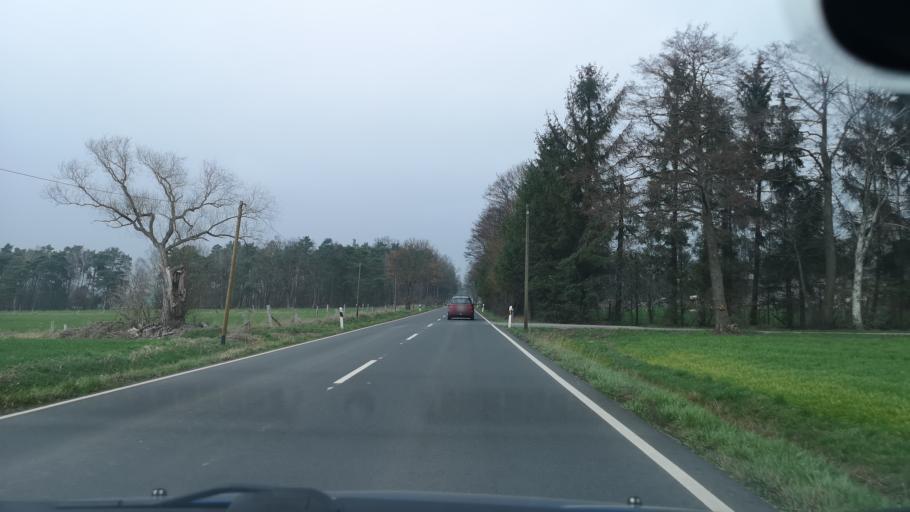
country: DE
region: Lower Saxony
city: Neustadt am Rubenberge
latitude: 52.4785
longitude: 9.5365
